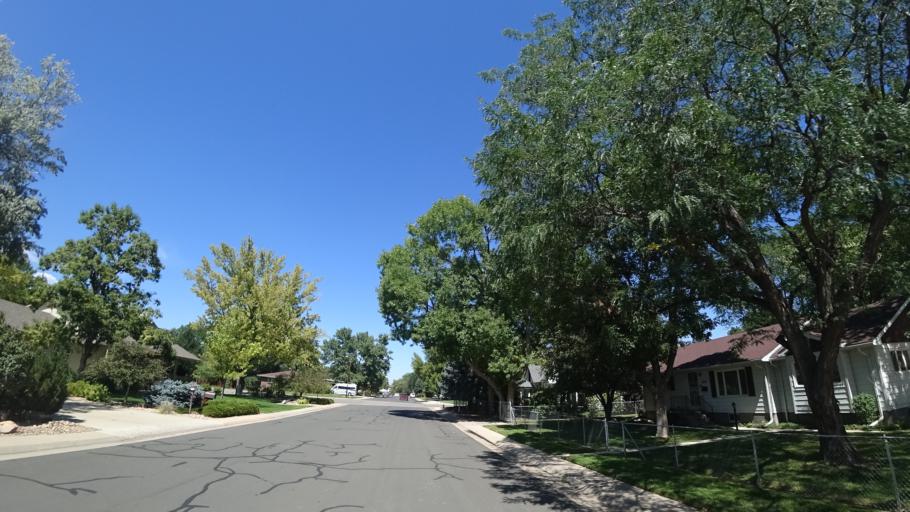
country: US
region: Colorado
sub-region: Arapahoe County
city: Greenwood Village
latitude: 39.6072
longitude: -104.9809
